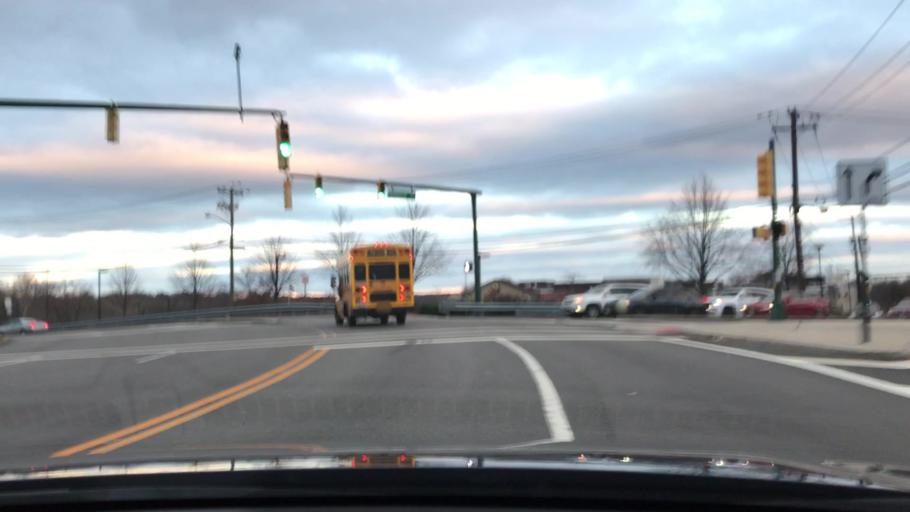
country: US
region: New Jersey
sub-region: Bergen County
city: Maywood
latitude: 40.9146
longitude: -74.0550
